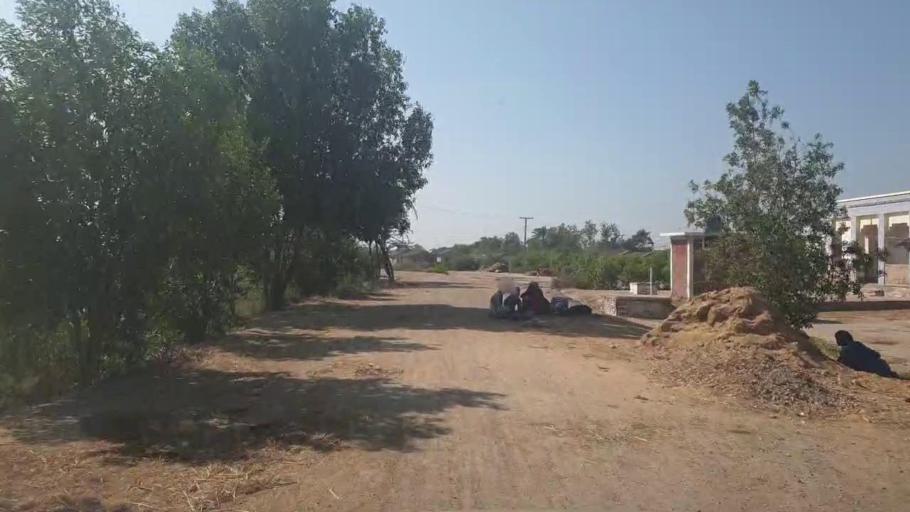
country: PK
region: Sindh
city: Badin
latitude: 24.5445
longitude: 68.8435
